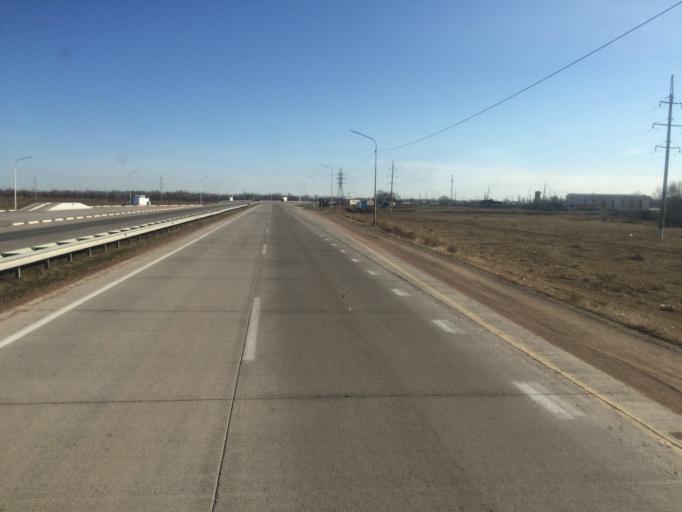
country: KG
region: Talas
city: Ivanovo-Alekseyevka
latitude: 42.9950
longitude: 72.0919
